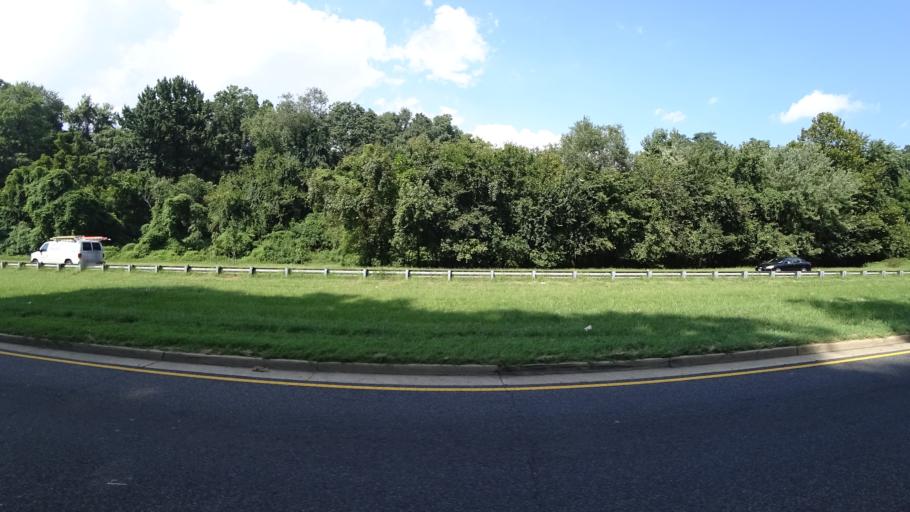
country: US
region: Maryland
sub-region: Prince George's County
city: Glassmanor
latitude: 38.8530
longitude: -76.9903
